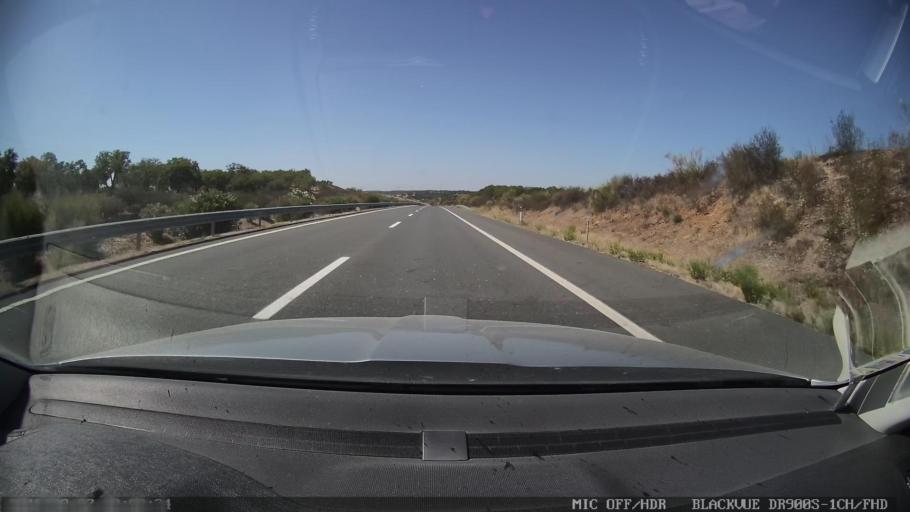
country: PT
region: Evora
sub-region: Evora
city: Evora
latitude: 38.7292
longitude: -7.7674
